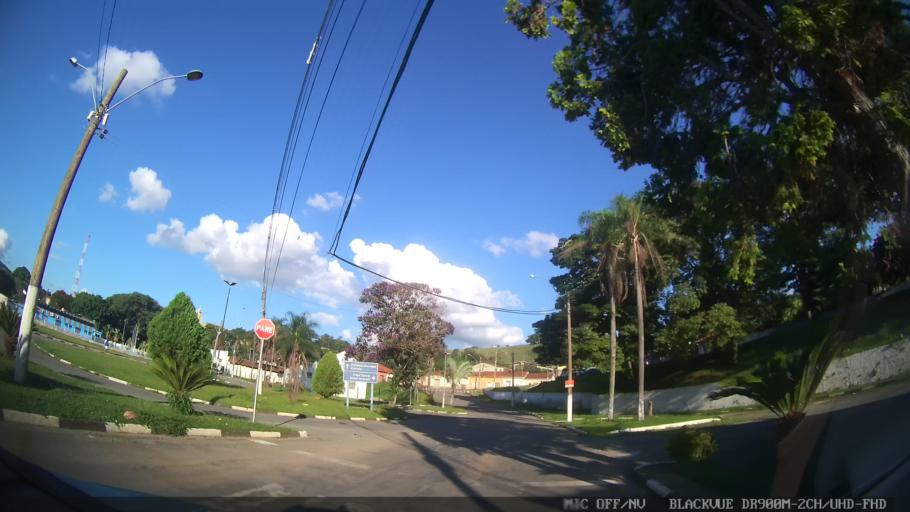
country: BR
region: Minas Gerais
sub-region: Extrema
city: Extrema
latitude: -22.8931
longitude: -46.4175
